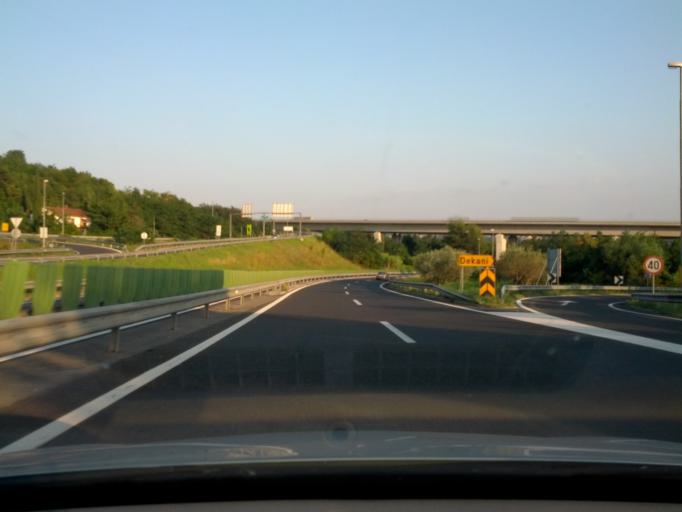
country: SI
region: Koper-Capodistria
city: Spodnje Skofije
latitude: 45.5617
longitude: 13.7847
